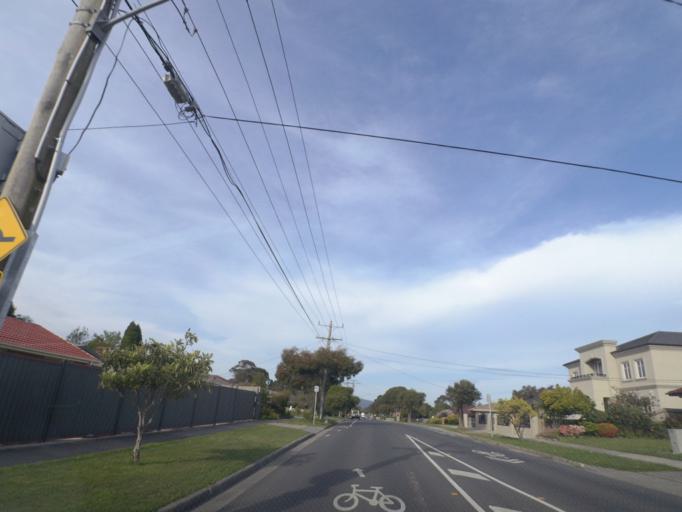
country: AU
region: Victoria
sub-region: Knox
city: Wantirna South
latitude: -37.8890
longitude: 145.2218
